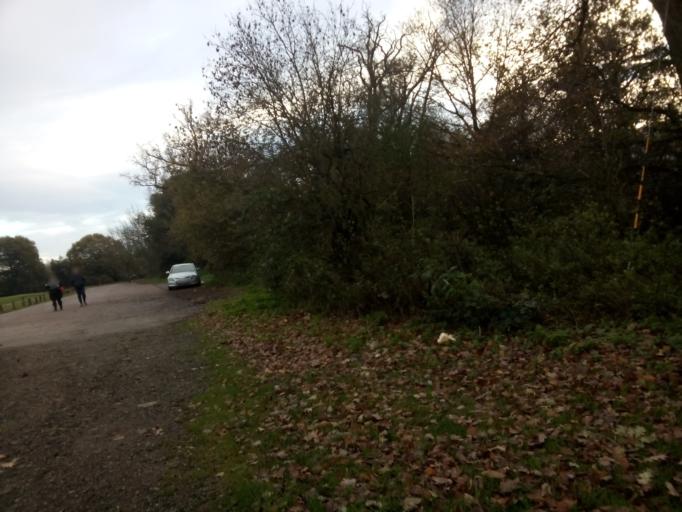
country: GB
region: England
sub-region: Suffolk
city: Bramford
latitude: 52.0513
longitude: 1.1158
